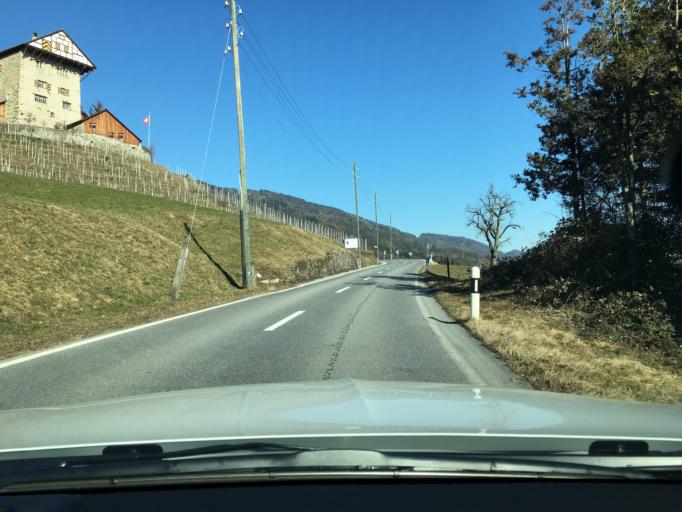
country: CH
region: Saint Gallen
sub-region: Wahlkreis Rheintal
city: Altstatten
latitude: 47.3888
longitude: 9.5491
